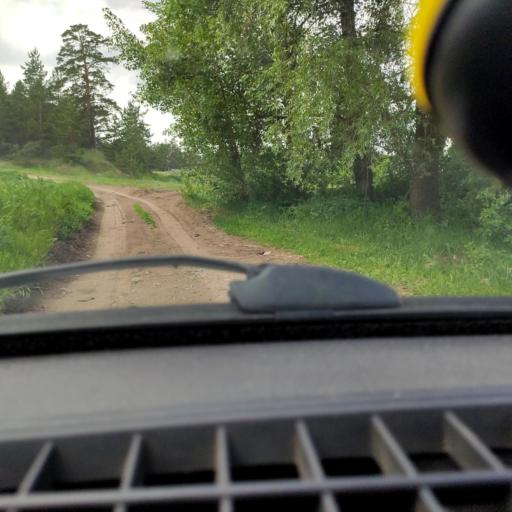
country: RU
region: Samara
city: Povolzhskiy
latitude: 53.6314
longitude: 49.6677
